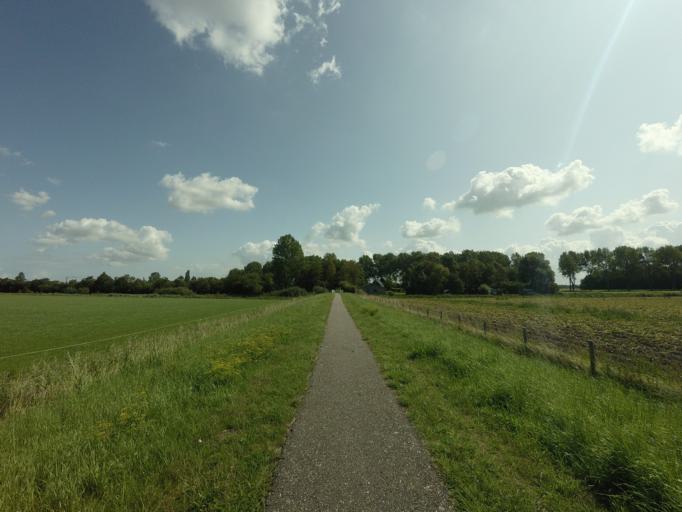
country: NL
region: Friesland
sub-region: Gemeente Leeuwarderadeel
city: Stiens
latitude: 53.2831
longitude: 5.7203
